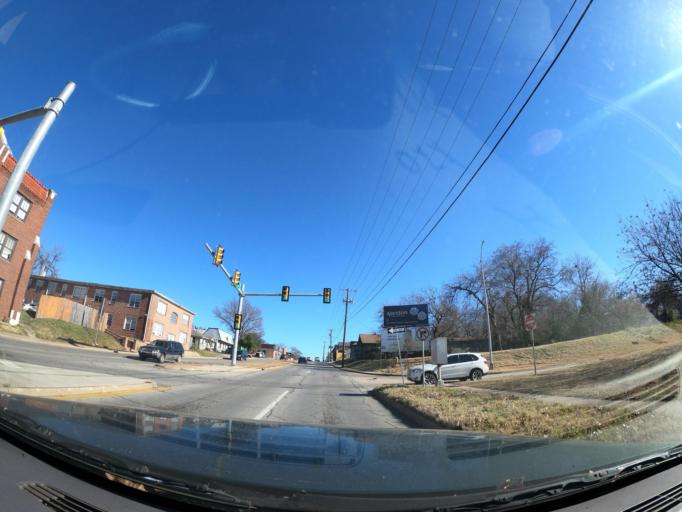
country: US
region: Oklahoma
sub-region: Tulsa County
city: Tulsa
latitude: 36.1404
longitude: -95.9537
